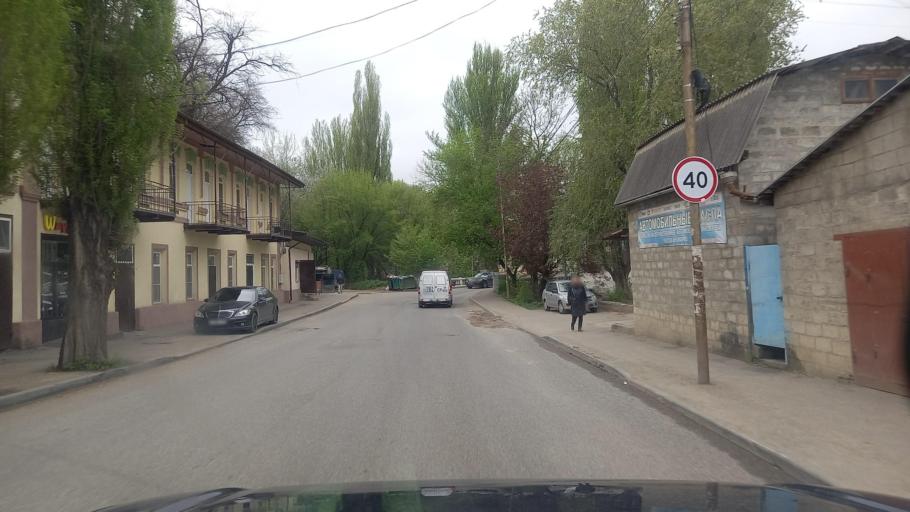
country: RU
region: Stavropol'skiy
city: Kislovodsk
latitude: 43.8946
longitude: 42.7127
